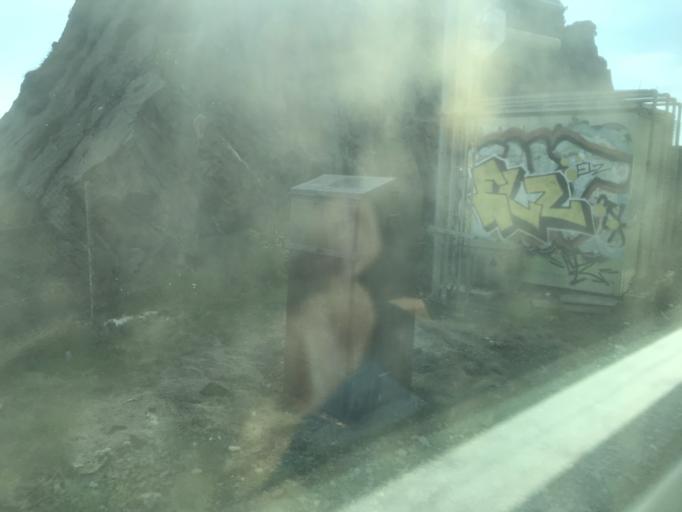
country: IE
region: Leinster
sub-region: Wicklow
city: Bray
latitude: 53.1904
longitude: -6.0787
